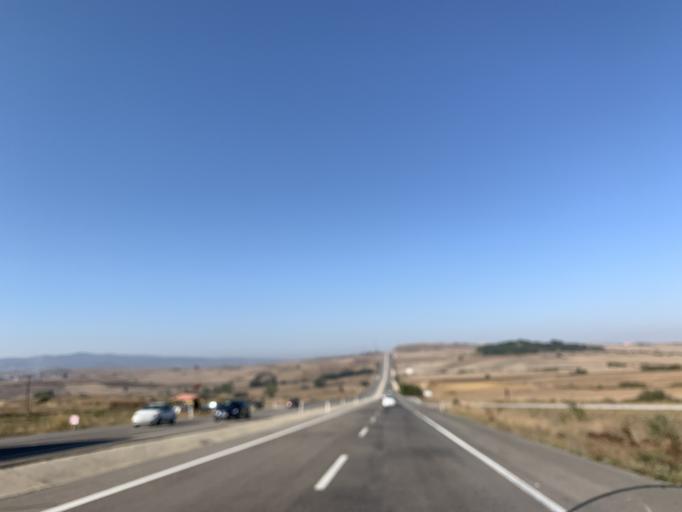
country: TR
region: Tekirdag
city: Balli
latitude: 40.8754
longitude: 27.0514
